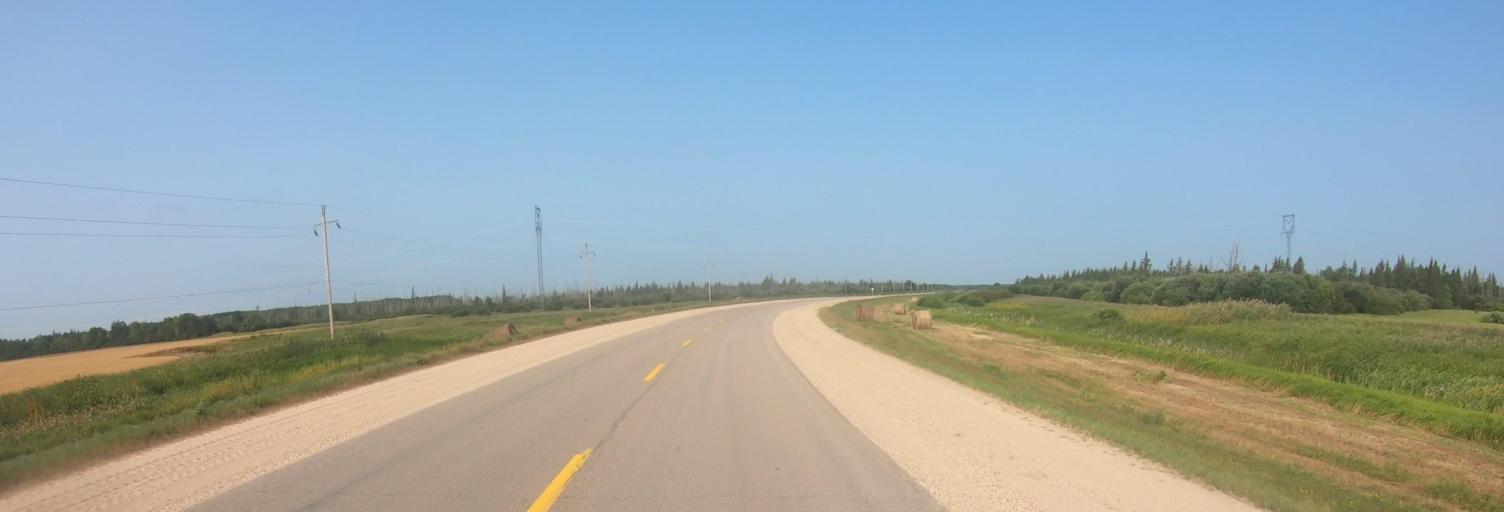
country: US
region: Minnesota
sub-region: Roseau County
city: Warroad
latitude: 49.0157
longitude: -95.5350
